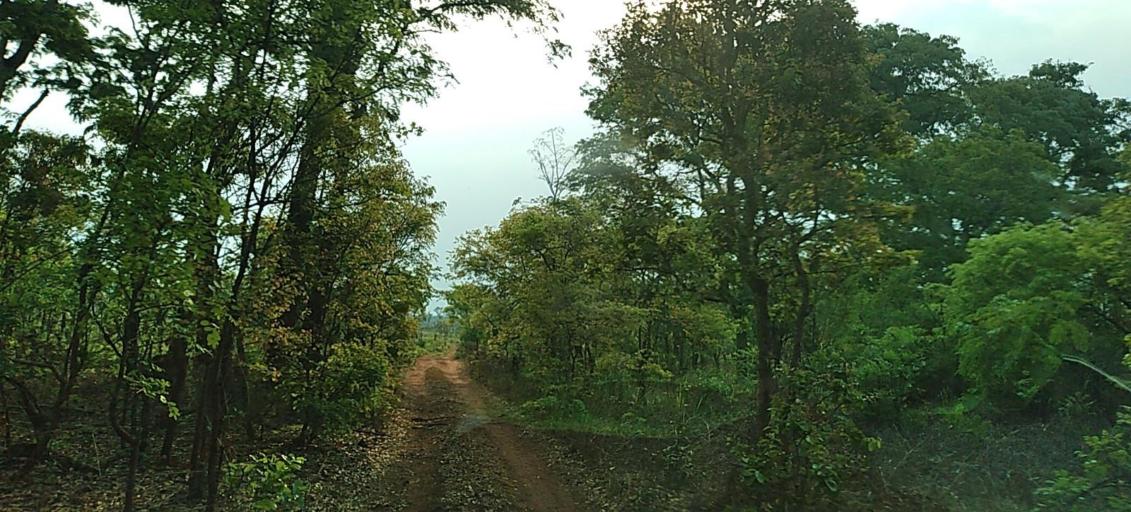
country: ZM
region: North-Western
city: Solwezi
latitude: -12.0419
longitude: 26.0347
